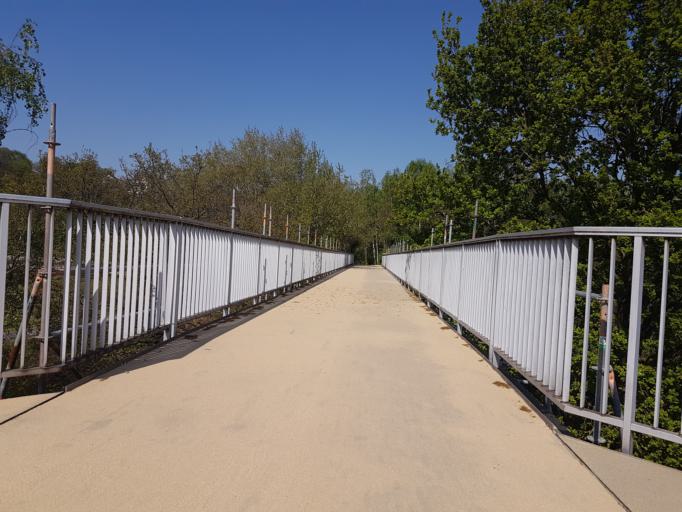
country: DE
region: North Rhine-Westphalia
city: Witten
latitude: 51.4321
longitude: 7.3156
